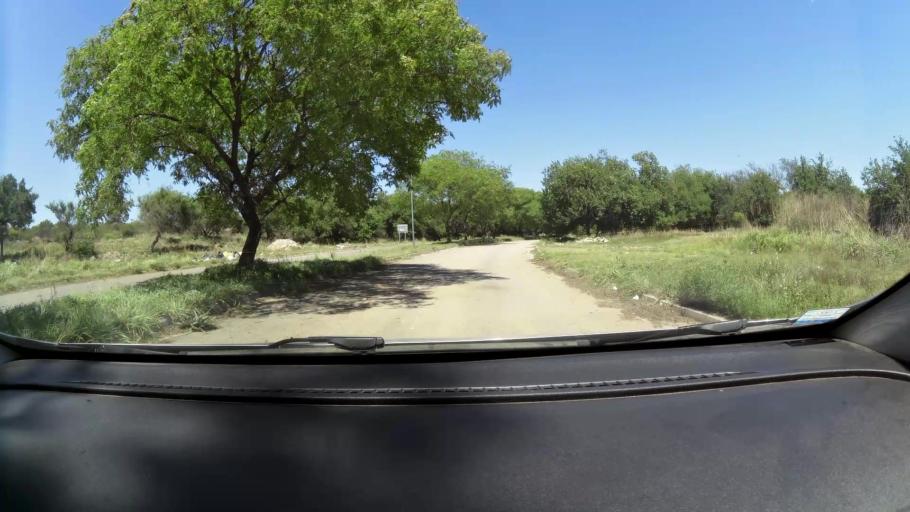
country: AR
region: Cordoba
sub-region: Departamento de Capital
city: Cordoba
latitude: -31.4094
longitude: -64.1287
